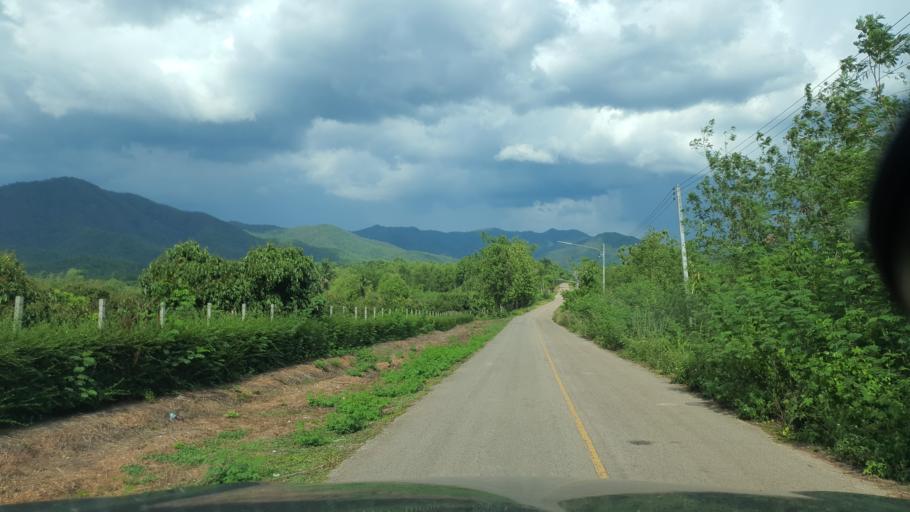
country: TH
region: Chiang Mai
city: Mae Taeng
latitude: 19.1311
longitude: 99.0445
